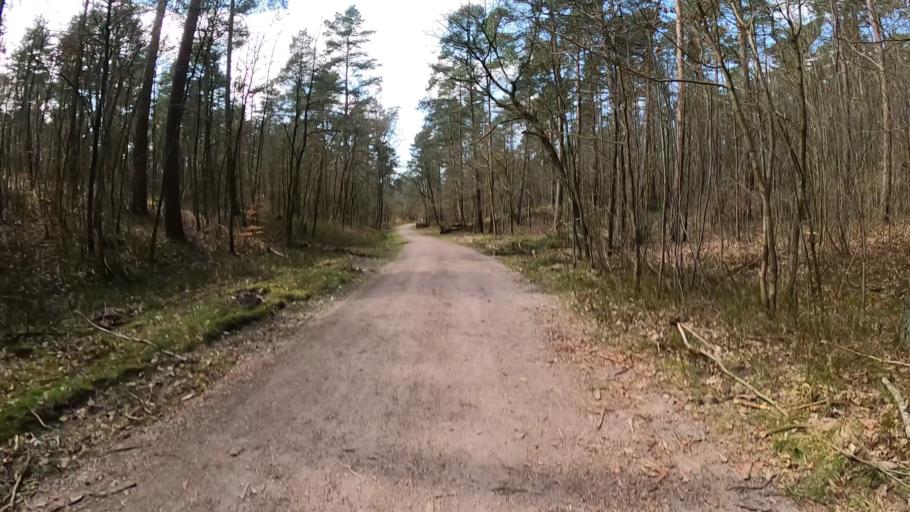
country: DE
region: Lower Saxony
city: Neu Wulmstorf
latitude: 53.4582
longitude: 9.8737
